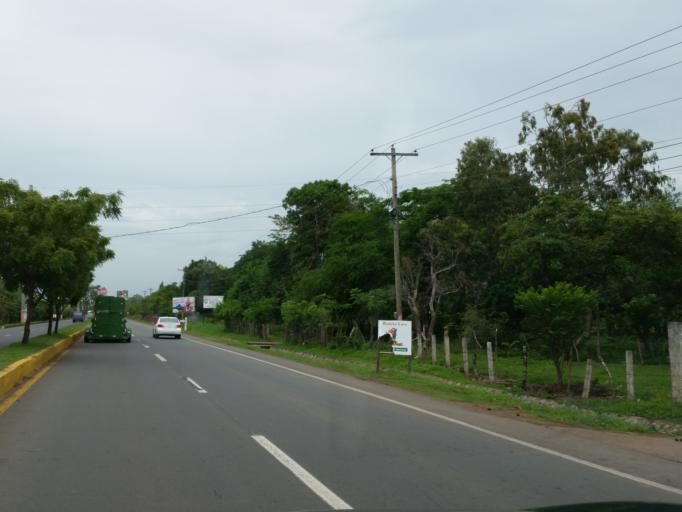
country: NI
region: Granada
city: Granada
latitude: 11.9427
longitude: -85.9789
